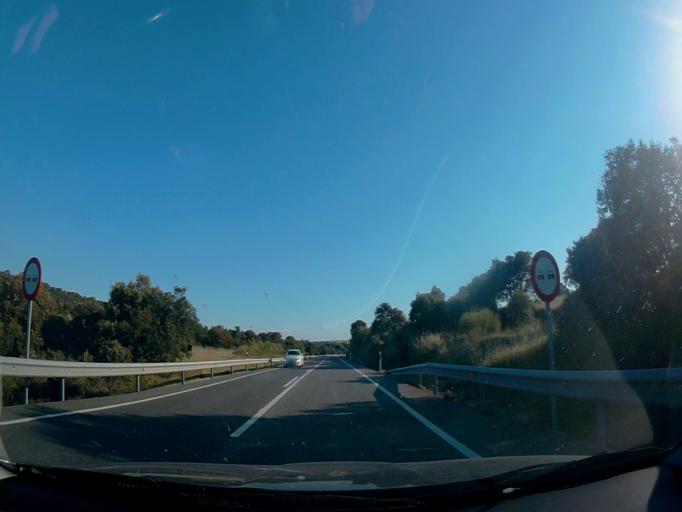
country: ES
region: Castille-La Mancha
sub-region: Province of Toledo
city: Paredes de Escalona
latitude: 40.1999
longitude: -4.3986
